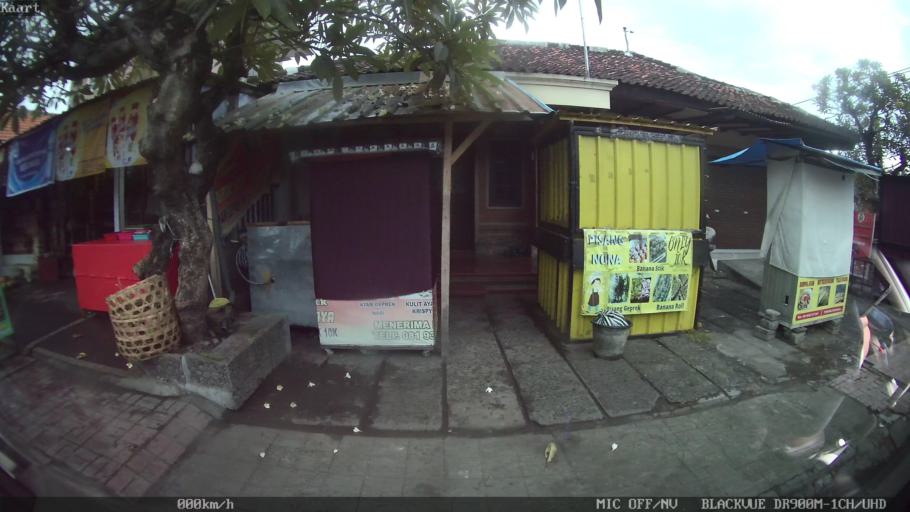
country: ID
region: Bali
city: Banjar Pasekan
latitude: -8.6141
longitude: 115.2837
